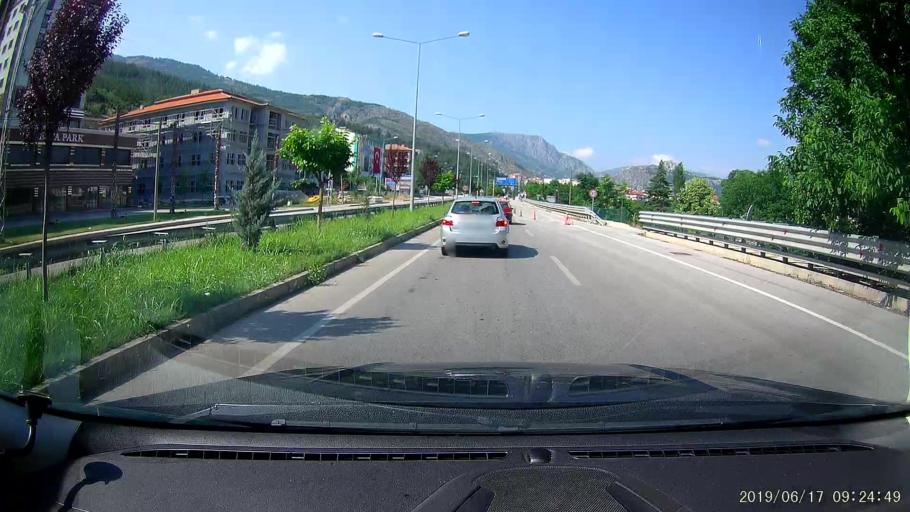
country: TR
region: Amasya
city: Amasya
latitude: 40.6699
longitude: 35.8533
